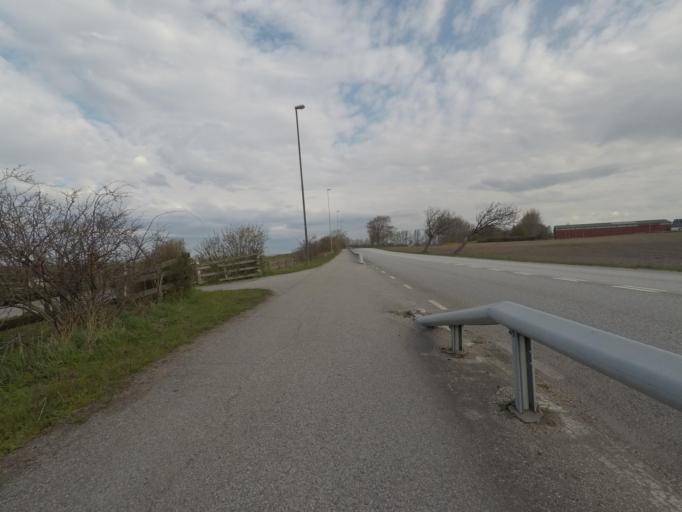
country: SE
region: Skane
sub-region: Burlovs Kommun
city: Arloev
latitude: 55.6506
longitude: 13.0559
